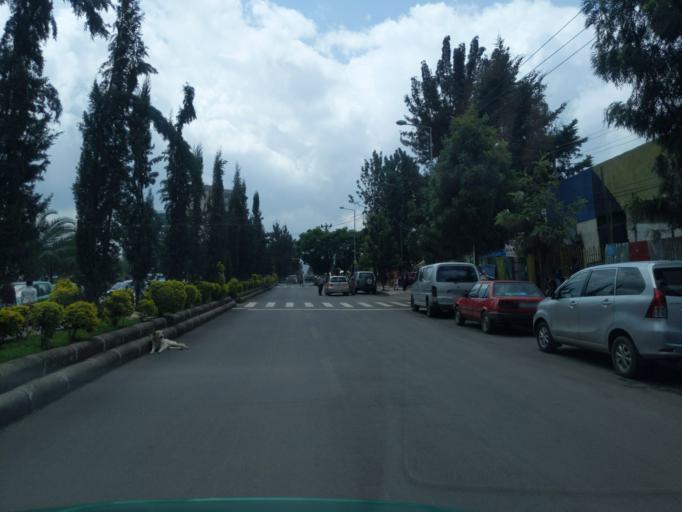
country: ET
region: Adis Abeba
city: Addis Ababa
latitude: 9.0151
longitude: 38.7700
